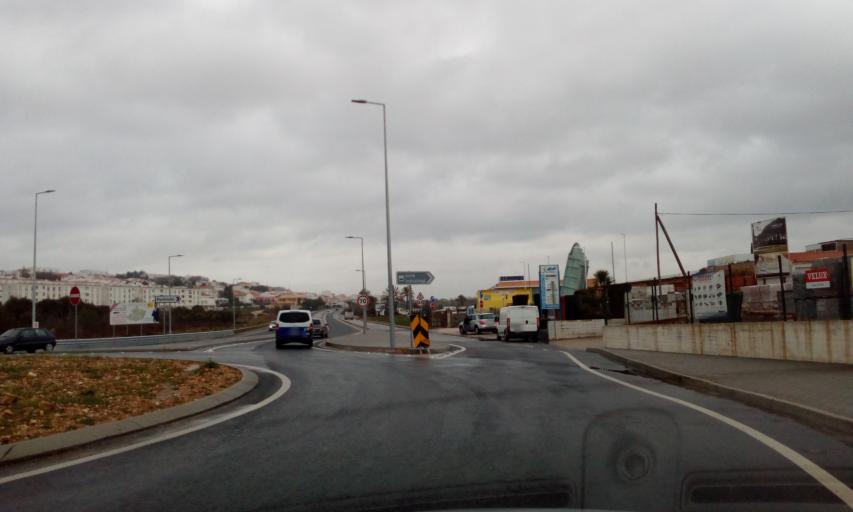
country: PT
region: Faro
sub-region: Lagos
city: Lagos
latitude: 37.1251
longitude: -8.6725
